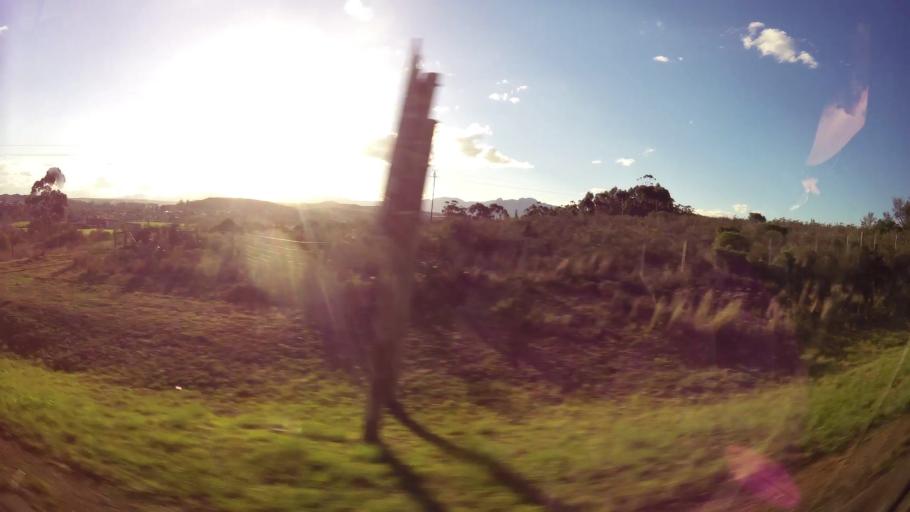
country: ZA
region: Western Cape
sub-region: Eden District Municipality
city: Riversdale
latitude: -34.0918
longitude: 20.9760
